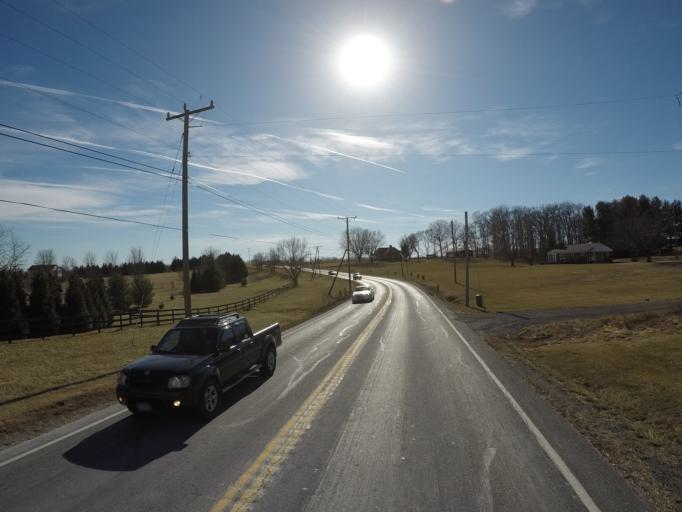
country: US
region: Maryland
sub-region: Frederick County
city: Point of Rocks
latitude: 39.2262
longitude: -77.5347
